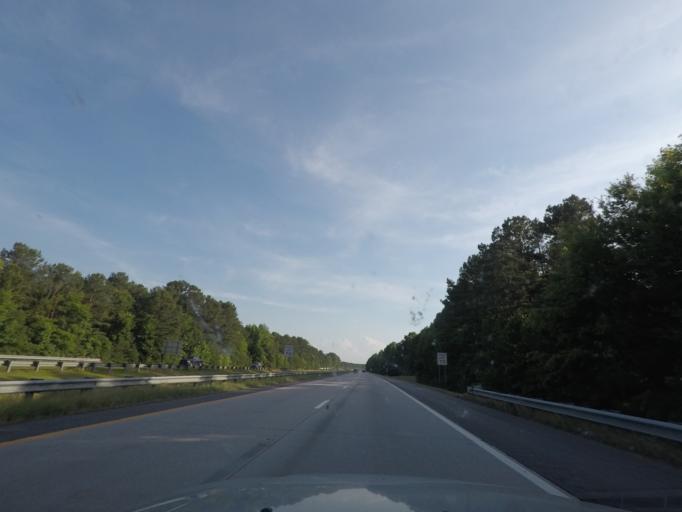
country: US
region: North Carolina
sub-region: Granville County
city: Oxford
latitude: 36.2633
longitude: -78.6147
